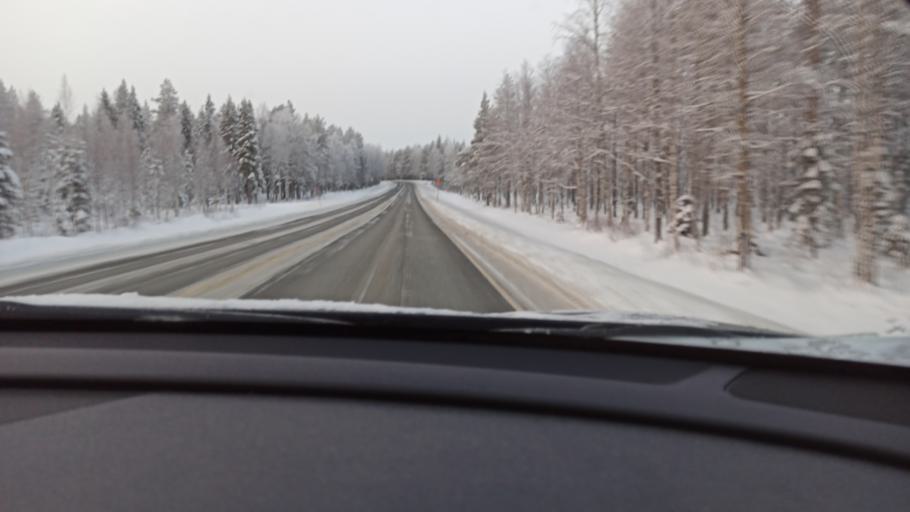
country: FI
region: Lapland
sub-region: Rovaniemi
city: Rovaniemi
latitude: 66.5615
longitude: 25.9200
